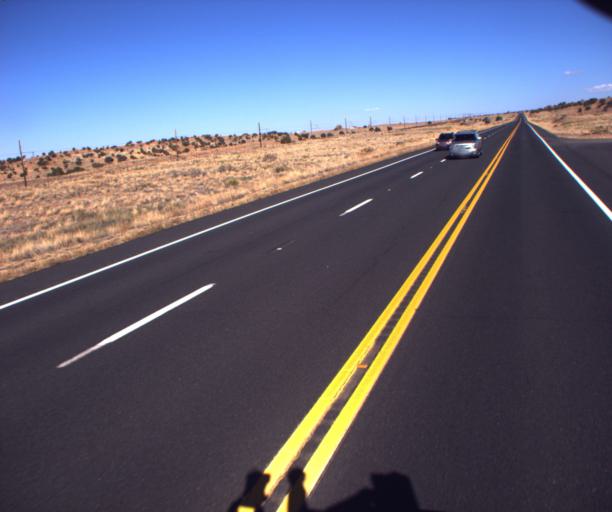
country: US
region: Arizona
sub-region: Coconino County
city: Kaibito
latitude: 36.4337
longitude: -110.7669
